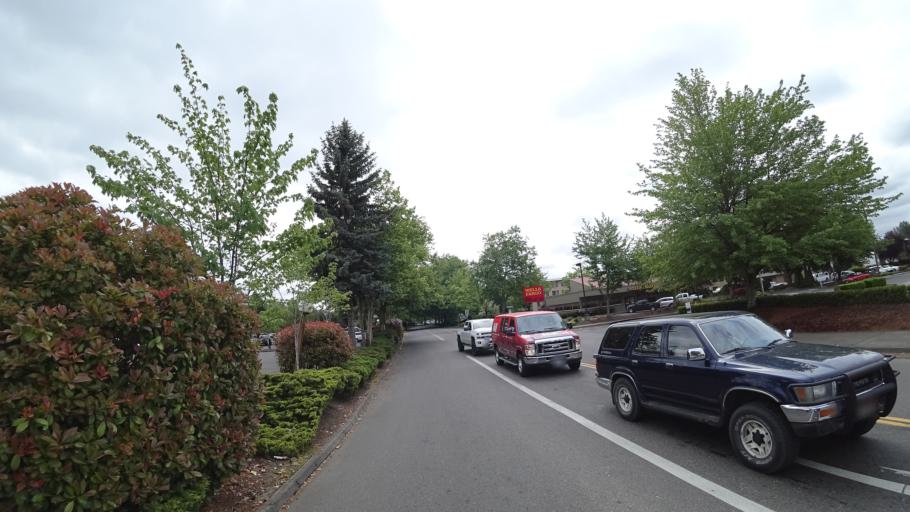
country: US
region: Washington
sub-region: Clark County
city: Vancouver
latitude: 45.6120
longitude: -122.6763
